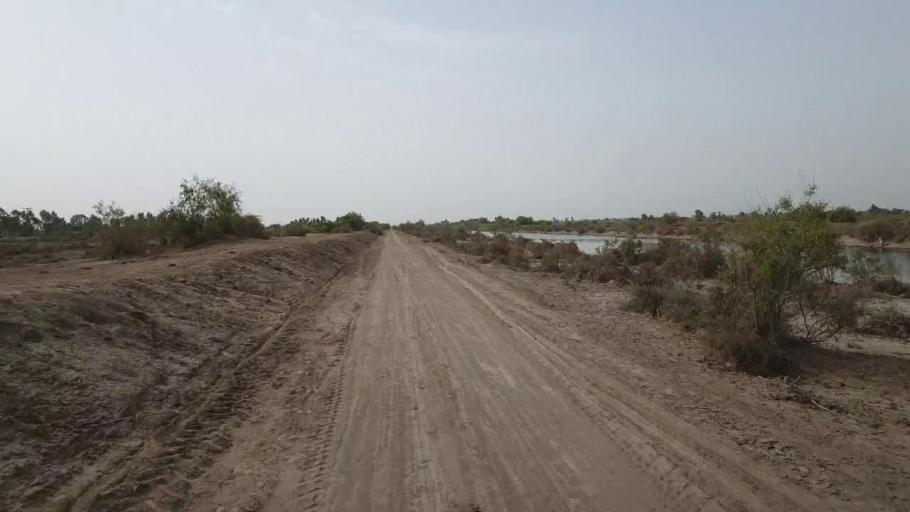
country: PK
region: Sindh
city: Daur
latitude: 26.4193
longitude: 68.1596
